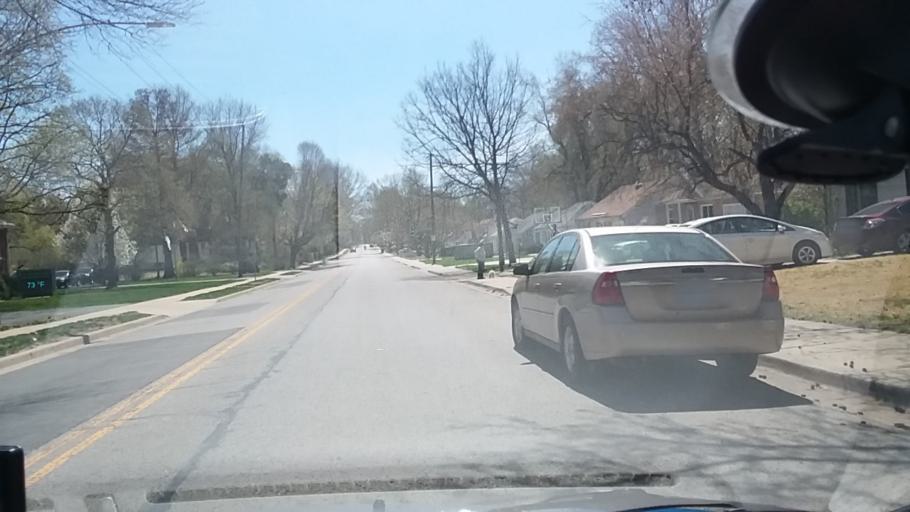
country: US
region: Kansas
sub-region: Johnson County
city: Westwood
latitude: 39.0405
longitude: -94.6212
